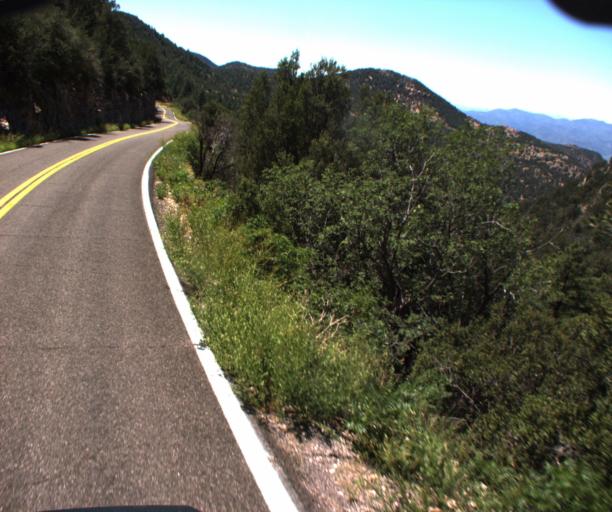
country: US
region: Arizona
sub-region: Greenlee County
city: Morenci
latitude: 33.1958
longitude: -109.3810
